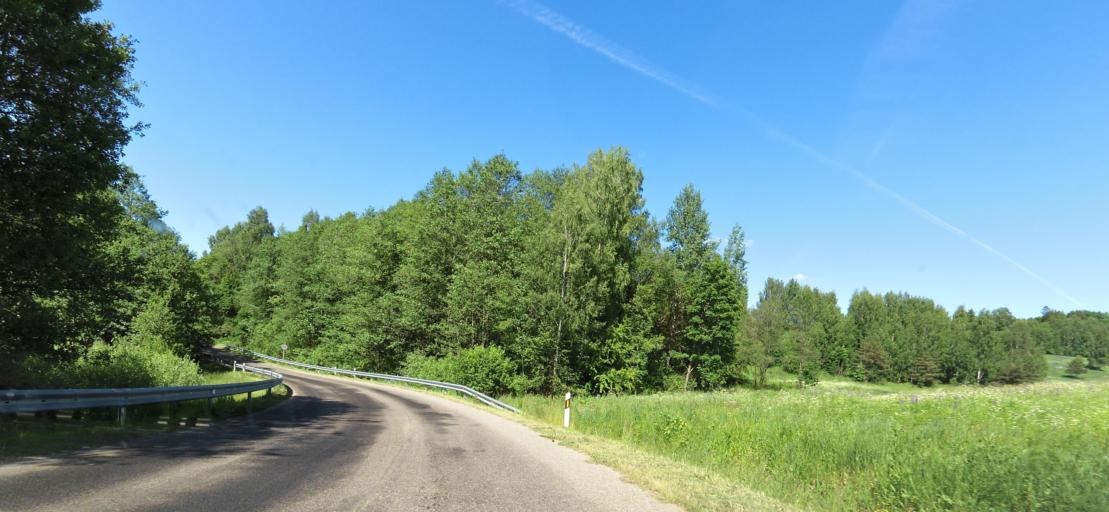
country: LT
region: Utenos apskritis
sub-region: Anyksciai
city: Anyksciai
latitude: 55.3240
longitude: 25.1326
